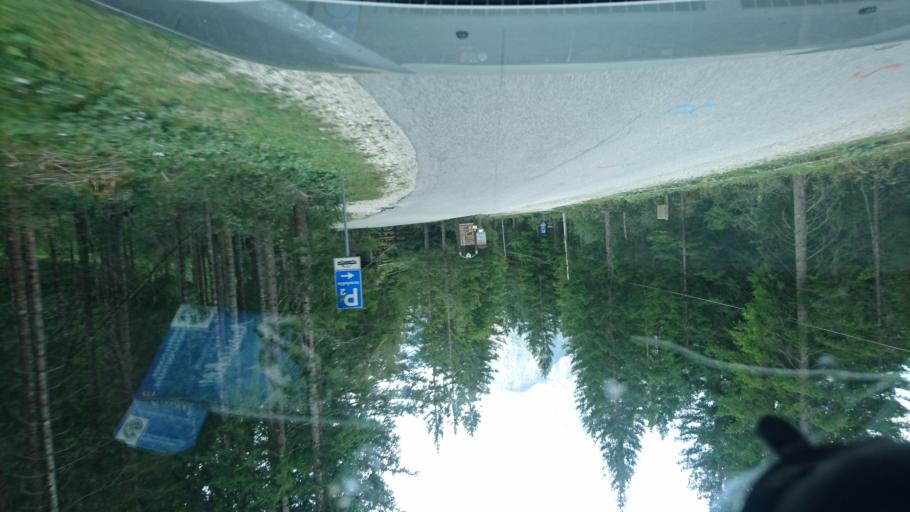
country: IT
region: Friuli Venezia Giulia
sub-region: Provincia di Udine
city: Malborghetto
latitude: 46.4717
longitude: 13.4925
